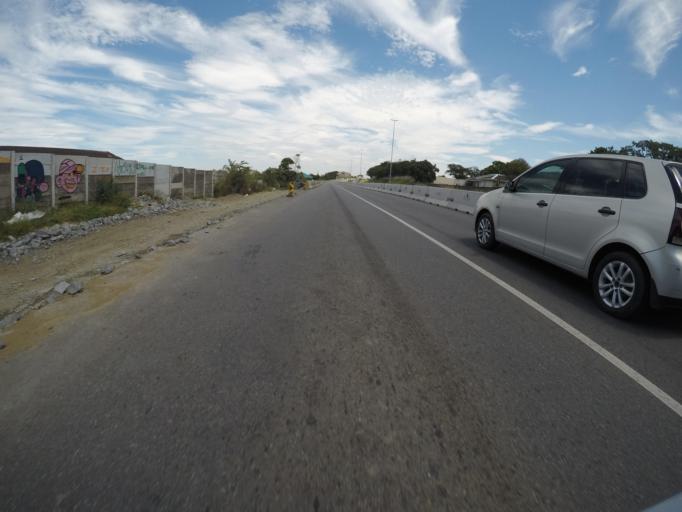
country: ZA
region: Eastern Cape
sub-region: Buffalo City Metropolitan Municipality
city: East London
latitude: -33.0362
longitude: 27.8614
